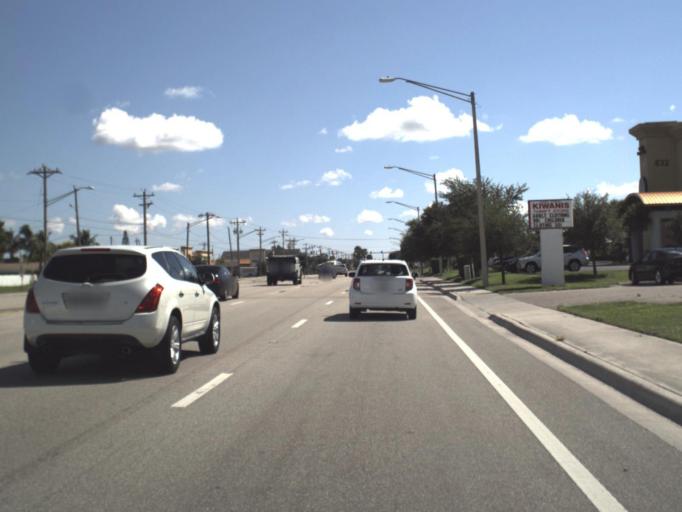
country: US
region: Florida
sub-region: Lee County
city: Lochmoor Waterway Estates
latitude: 26.6657
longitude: -81.9412
